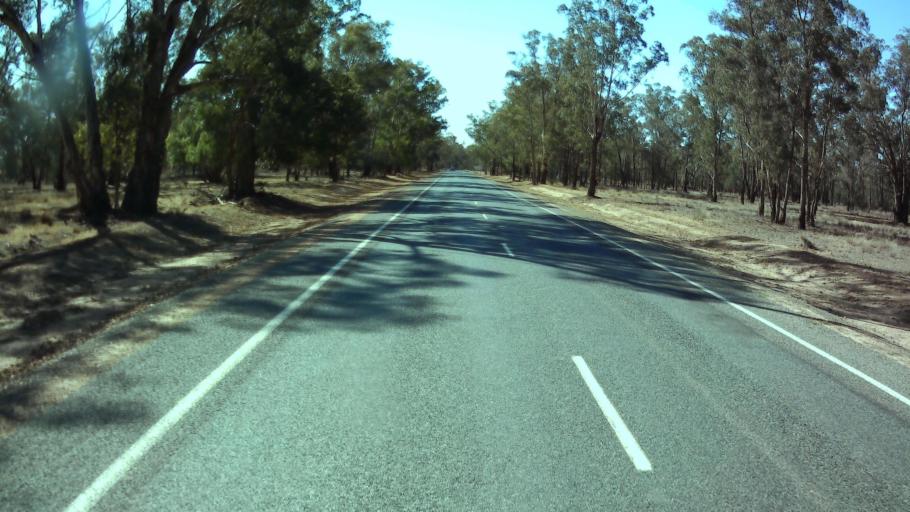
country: AU
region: New South Wales
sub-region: Weddin
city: Grenfell
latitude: -33.7241
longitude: 148.0846
